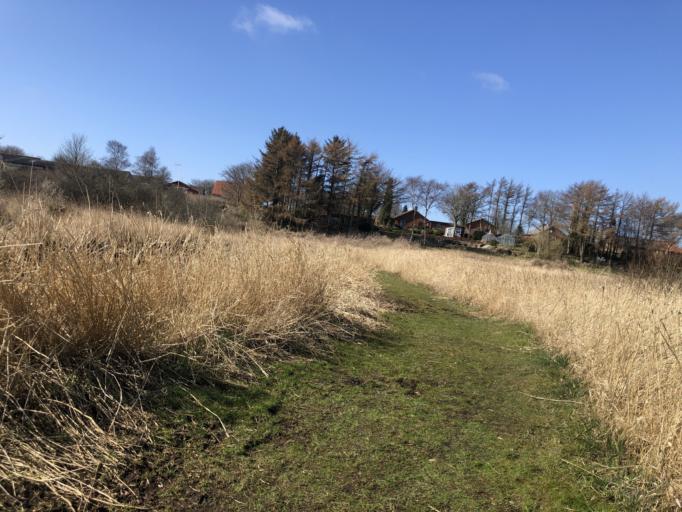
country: DK
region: Central Jutland
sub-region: Lemvig Kommune
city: Lemvig
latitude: 56.4157
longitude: 8.3116
